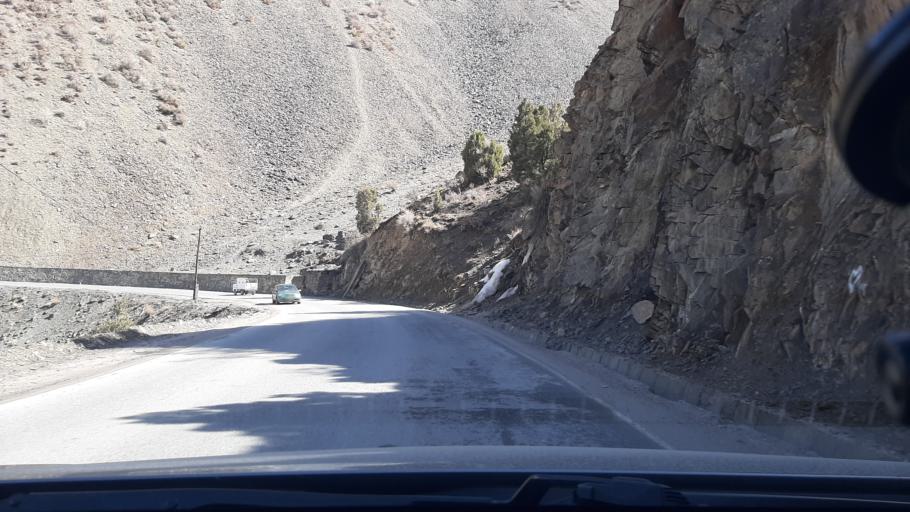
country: TJ
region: Viloyati Sughd
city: Ayni
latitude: 39.4998
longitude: 68.5530
